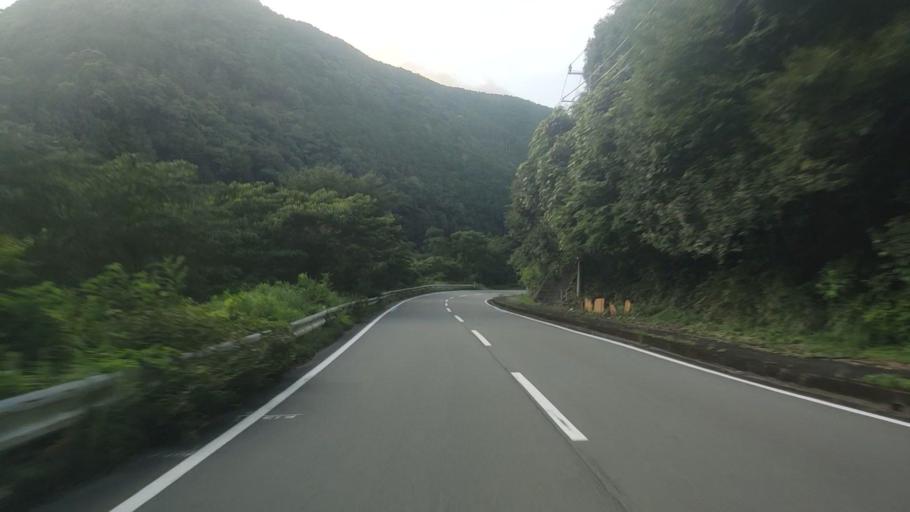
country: JP
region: Wakayama
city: Shingu
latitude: 33.8188
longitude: 135.7678
